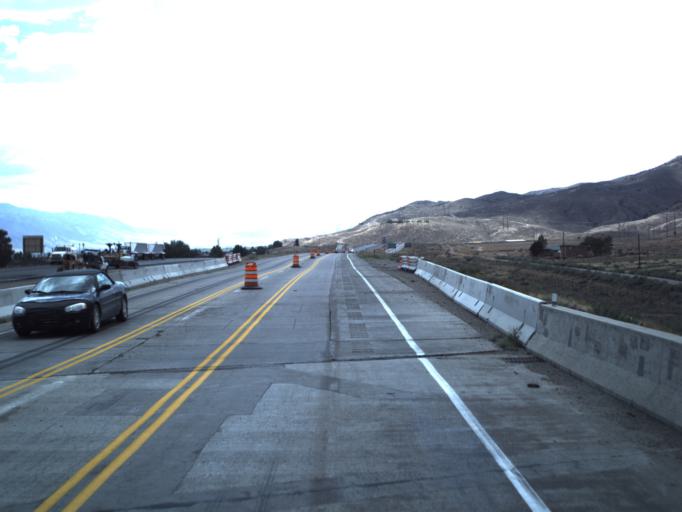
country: US
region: Utah
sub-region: Sevier County
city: Richfield
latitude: 38.7722
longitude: -112.0993
